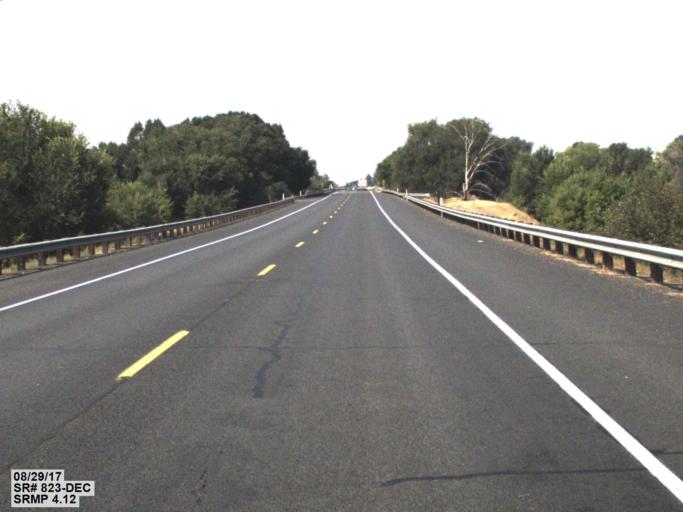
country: US
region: Washington
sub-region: Yakima County
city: Selah
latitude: 46.6794
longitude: -120.4948
